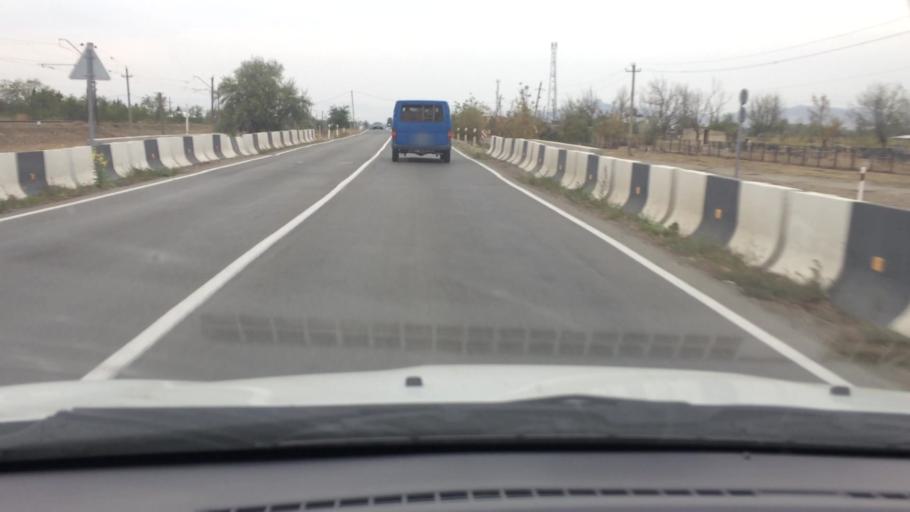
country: GE
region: Kvemo Kartli
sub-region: Marneuli
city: Marneuli
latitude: 41.4405
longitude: 44.8174
